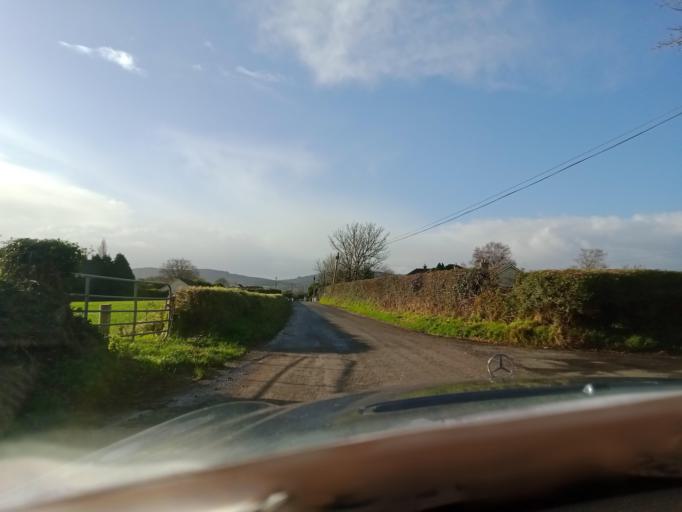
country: IE
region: Leinster
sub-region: Kilkenny
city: Mooncoin
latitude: 52.2923
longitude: -7.2665
